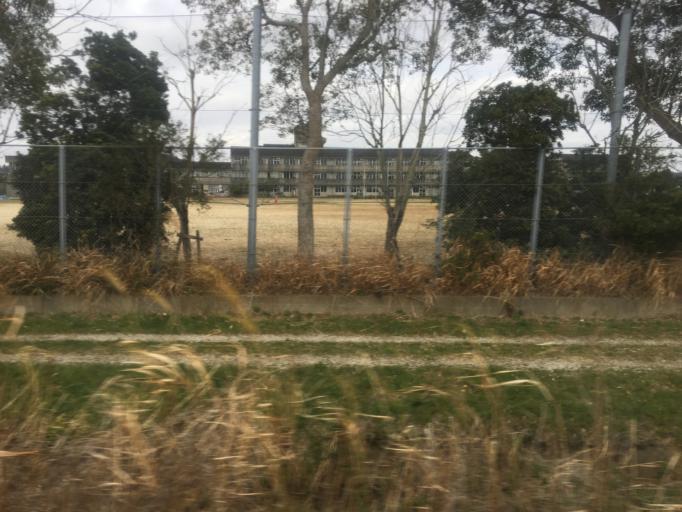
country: JP
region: Chiba
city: Togane
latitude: 35.5698
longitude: 140.3827
